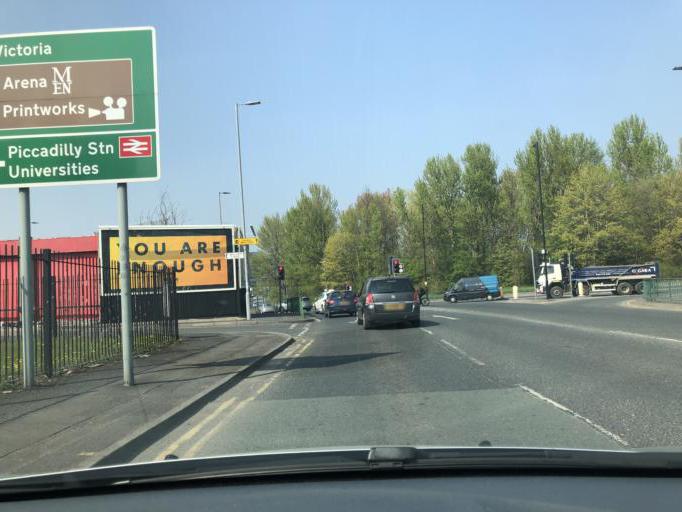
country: GB
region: England
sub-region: Manchester
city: Manchester
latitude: 53.4748
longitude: -2.2167
